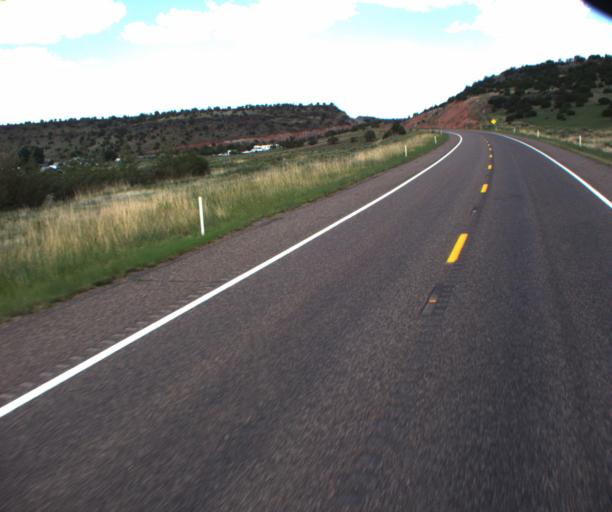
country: US
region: Arizona
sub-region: Apache County
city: Springerville
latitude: 34.1335
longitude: -109.2381
